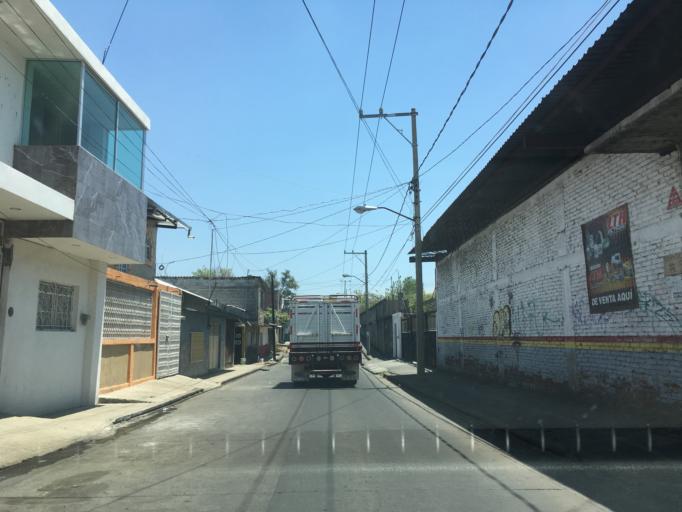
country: MX
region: Michoacan
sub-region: Uruapan
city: Uruapan
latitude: 19.4120
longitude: -102.0624
